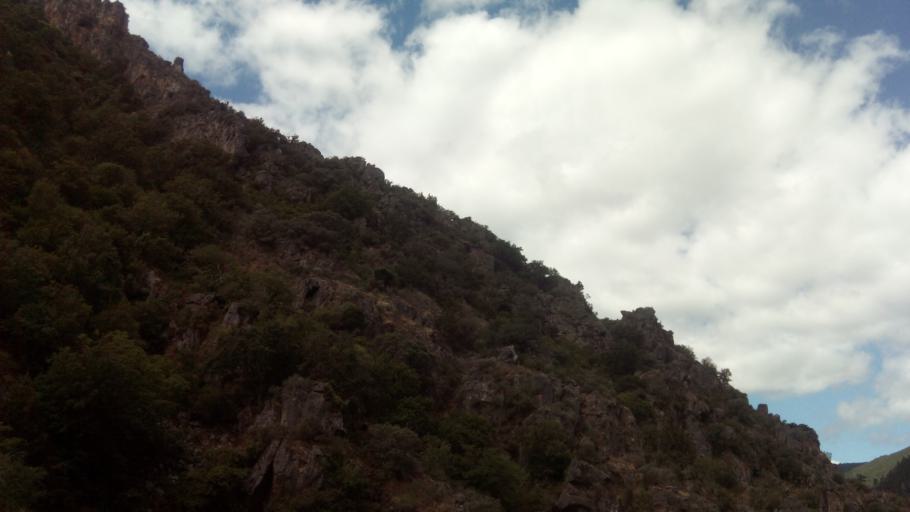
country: ES
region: Galicia
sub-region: Provincia de Lugo
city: Sober
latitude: 42.4034
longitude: -7.6300
